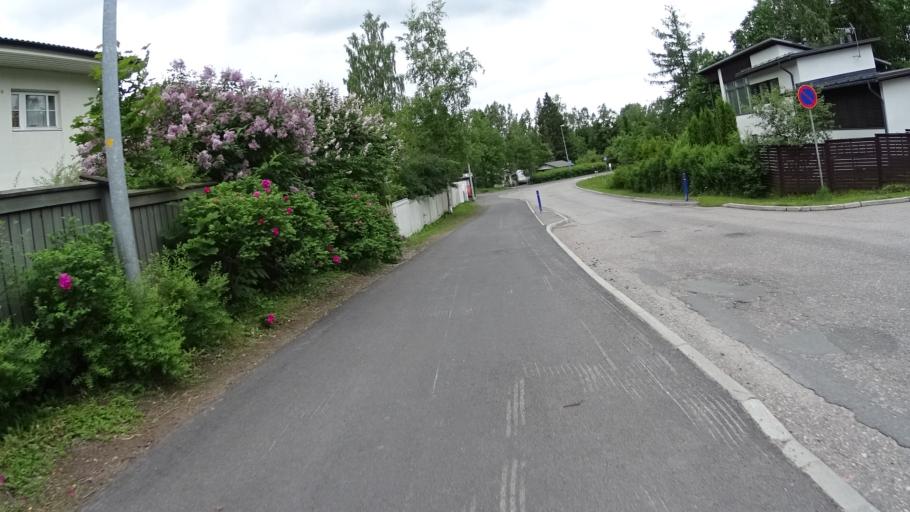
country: FI
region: Uusimaa
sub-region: Helsinki
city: Kilo
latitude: 60.2555
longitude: 24.7671
